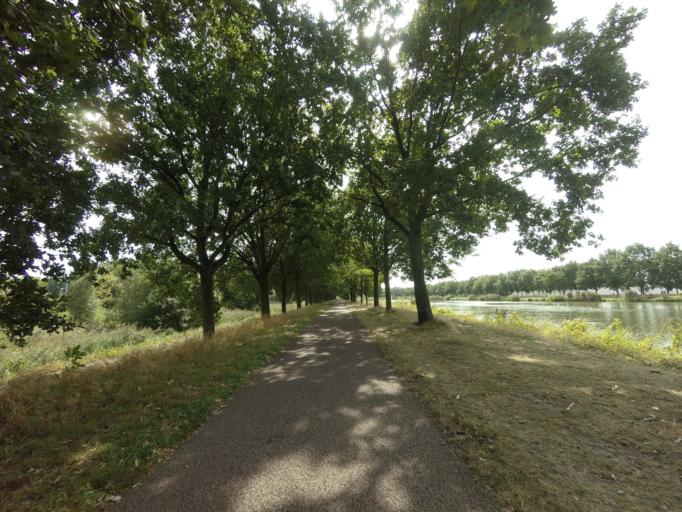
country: NL
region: North Brabant
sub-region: Gemeente Helmond
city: Helmond
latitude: 51.4556
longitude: 5.6948
